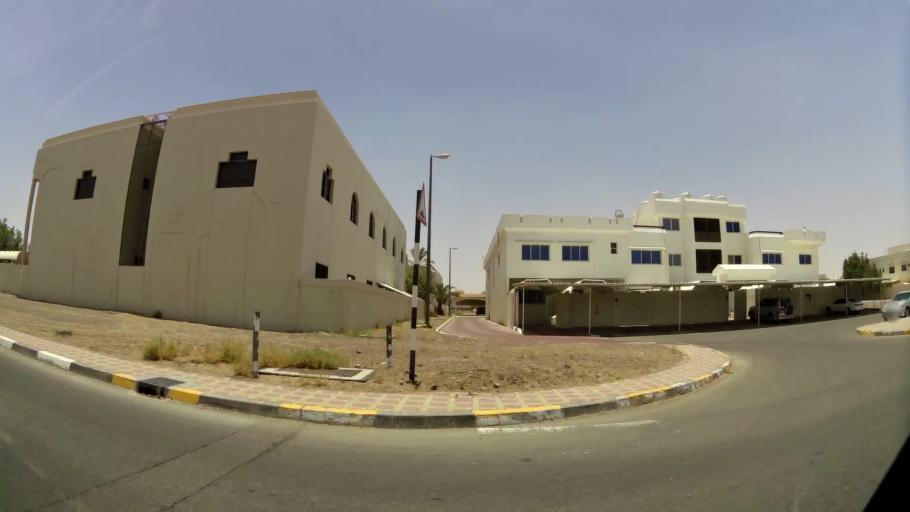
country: OM
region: Al Buraimi
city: Al Buraymi
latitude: 24.2602
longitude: 55.7248
